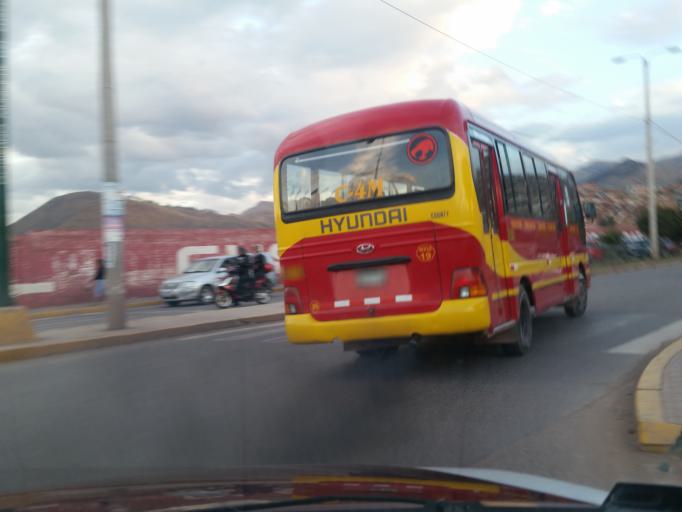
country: PE
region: Cusco
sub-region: Provincia de Cusco
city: Cusco
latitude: -13.5333
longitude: -71.9554
